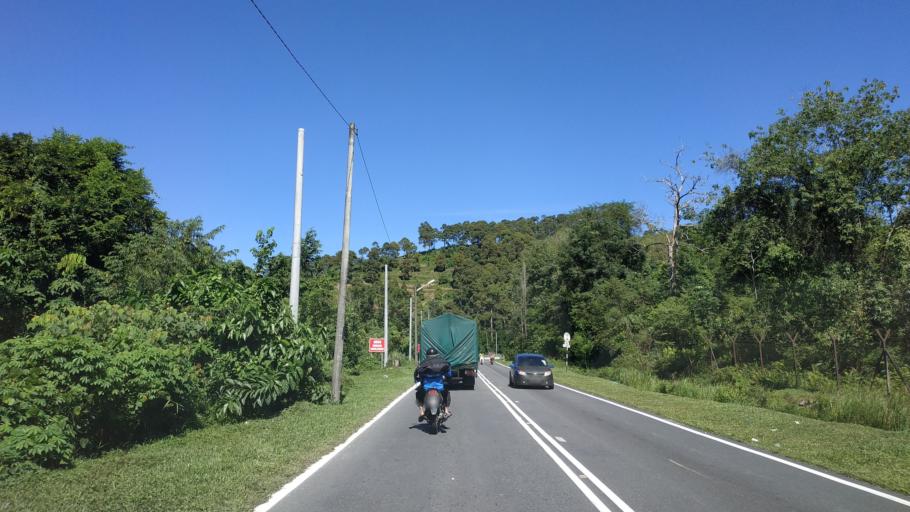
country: MY
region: Kedah
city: Kulim
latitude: 5.3260
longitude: 100.5330
